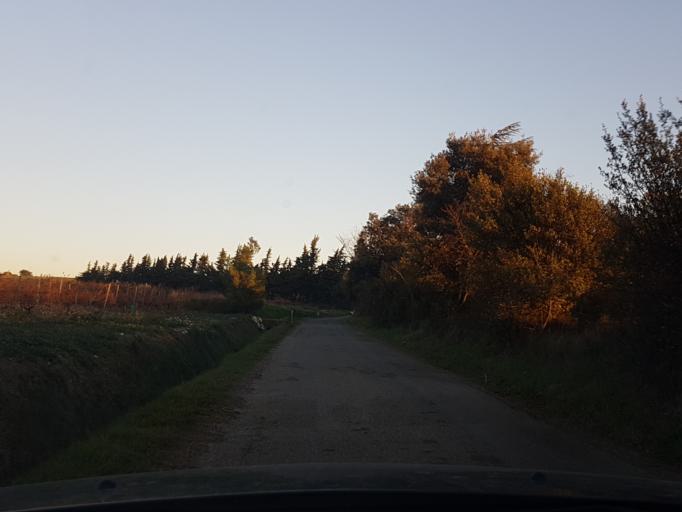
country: FR
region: Provence-Alpes-Cote d'Azur
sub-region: Departement du Vaucluse
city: Vedene
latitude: 43.9638
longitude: 4.9084
